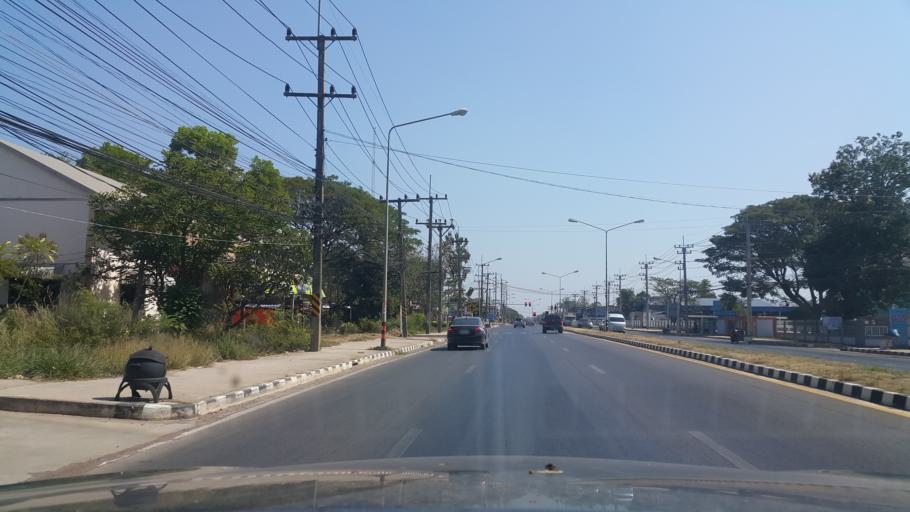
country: TH
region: Changwat Udon Thani
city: Nong Han
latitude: 17.3620
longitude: 103.1753
